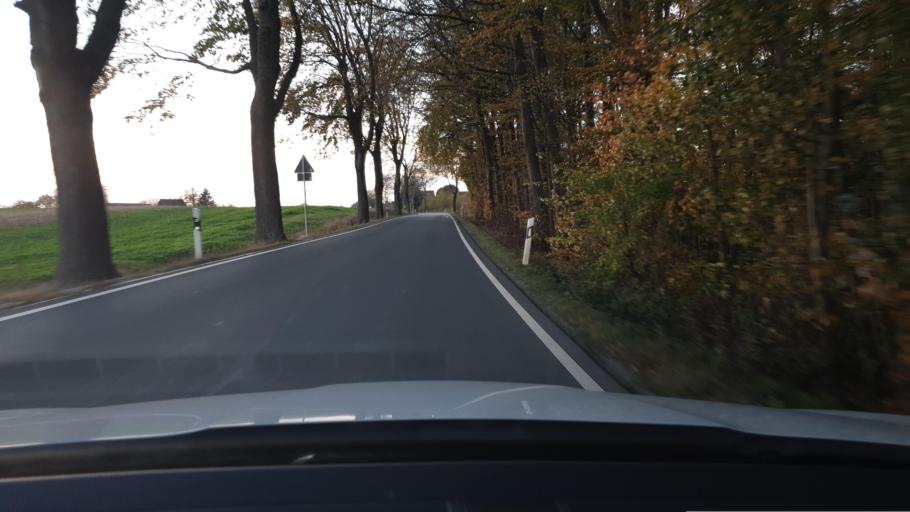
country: DE
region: North Rhine-Westphalia
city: Spenge
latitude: 52.0978
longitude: 8.4665
